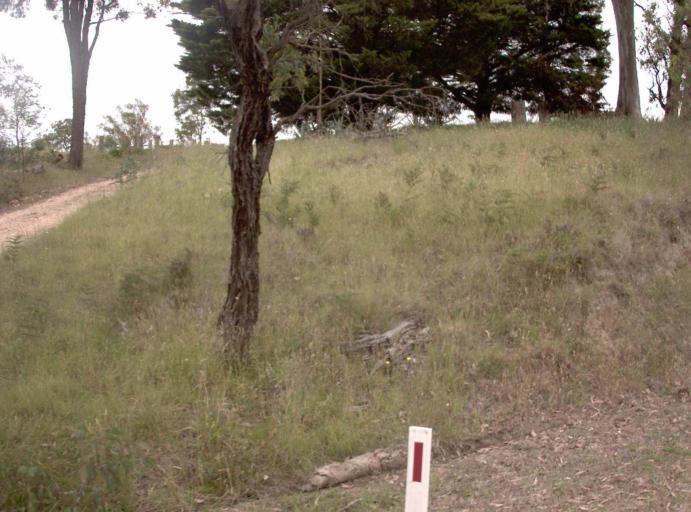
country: AU
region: Victoria
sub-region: East Gippsland
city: Bairnsdale
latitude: -37.7777
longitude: 147.3236
